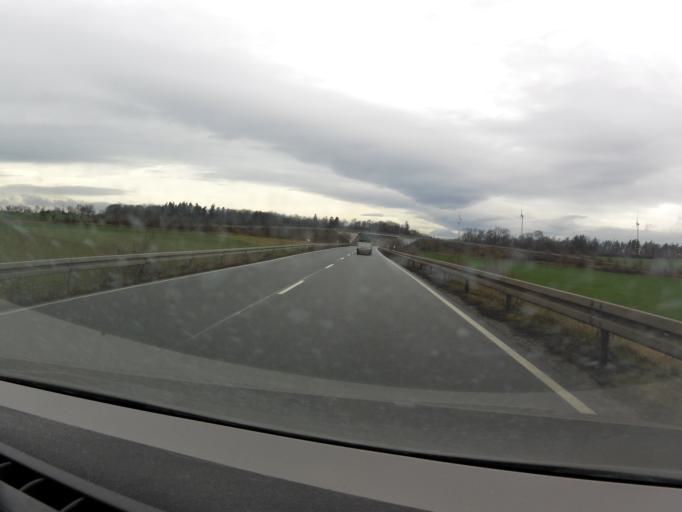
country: DE
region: Saxony-Anhalt
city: Grossorner
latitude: 51.6545
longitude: 11.4632
